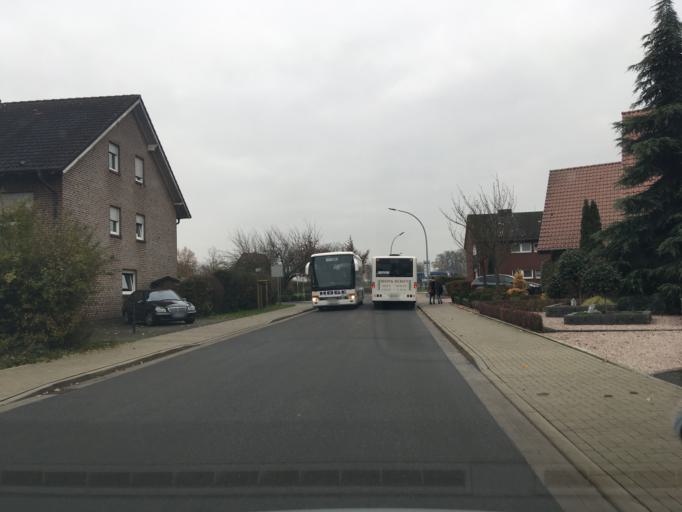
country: DE
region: North Rhine-Westphalia
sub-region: Regierungsbezirk Munster
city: Legden
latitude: 52.0283
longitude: 7.1050
